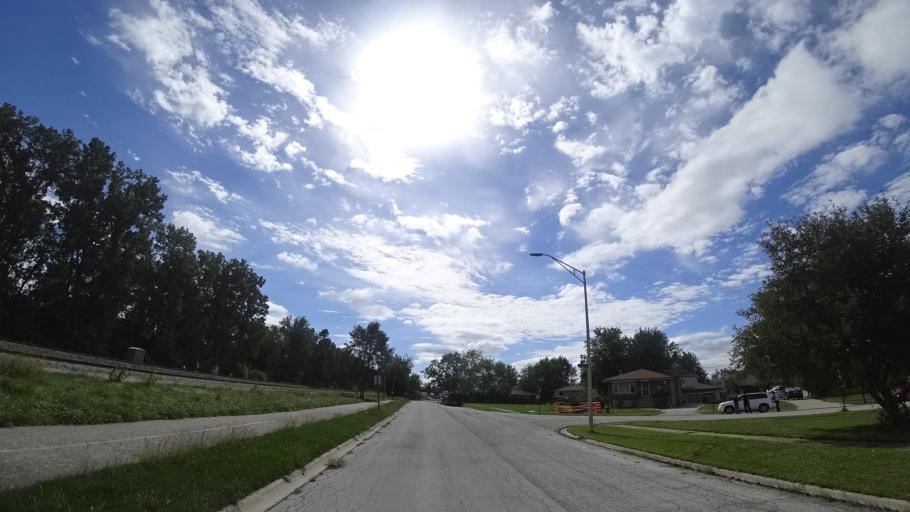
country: US
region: Illinois
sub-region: Cook County
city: Chicago Ridge
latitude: 41.7094
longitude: -87.7730
